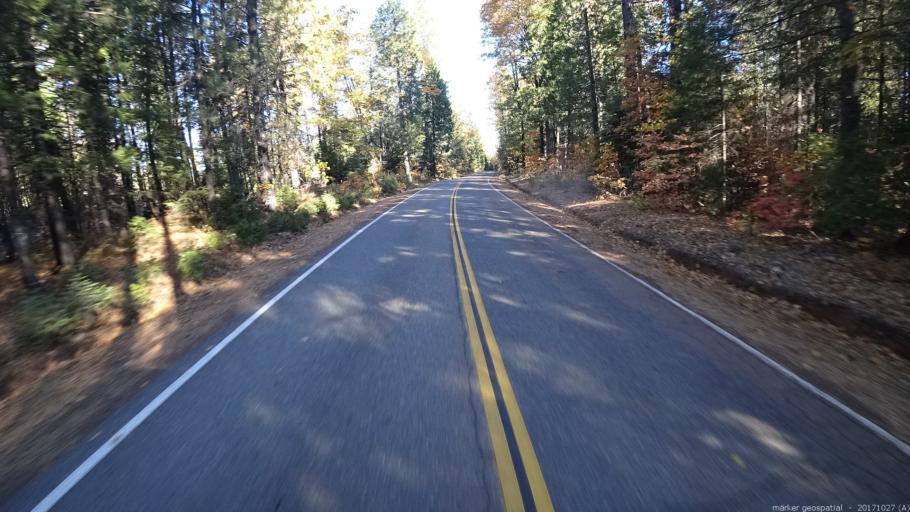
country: US
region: California
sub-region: Shasta County
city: Burney
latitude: 40.9735
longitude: -121.9306
